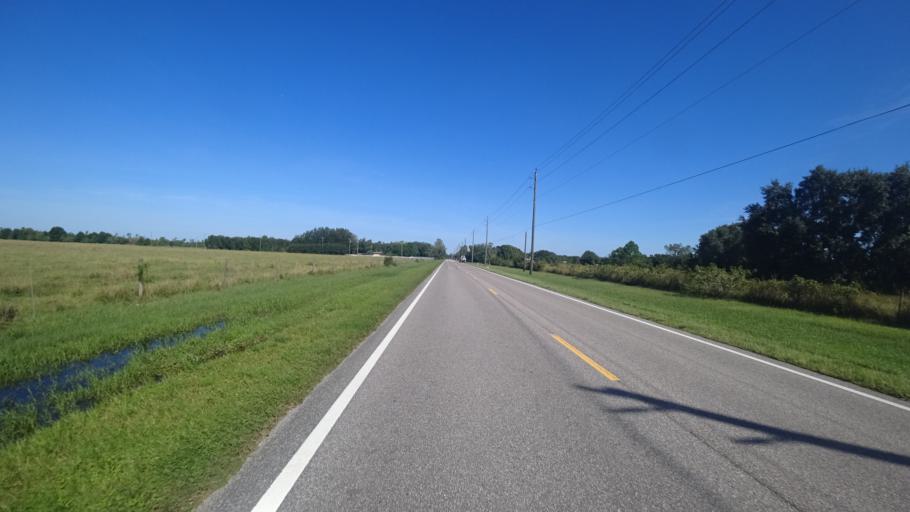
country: US
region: Florida
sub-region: Sarasota County
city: Lake Sarasota
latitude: 27.3765
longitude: -82.2683
